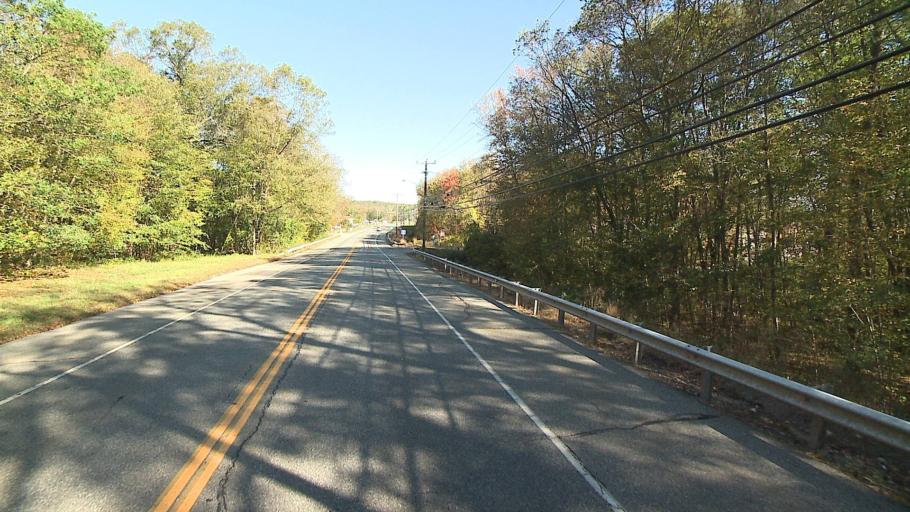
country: US
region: Connecticut
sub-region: Hartford County
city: Terramuggus
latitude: 41.6266
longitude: -72.4622
